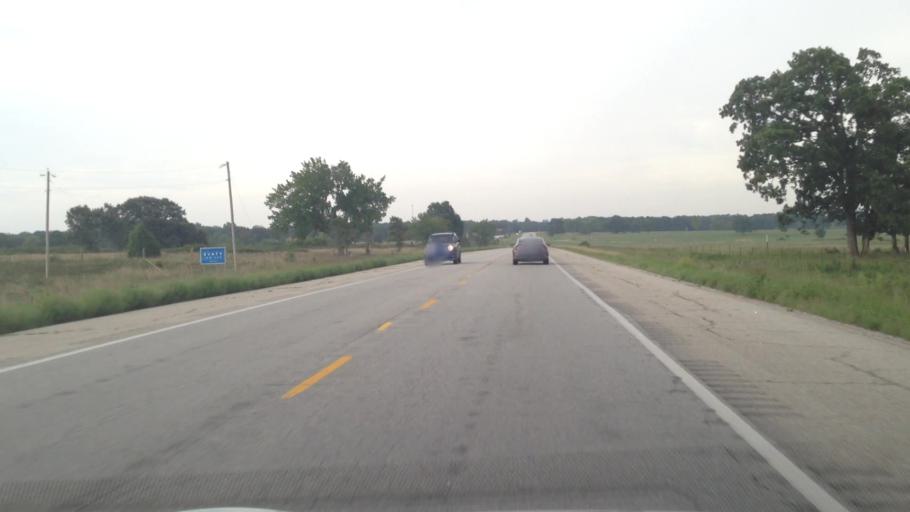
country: US
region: Kansas
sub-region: Cherokee County
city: Galena
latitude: 37.0134
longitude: -94.6301
